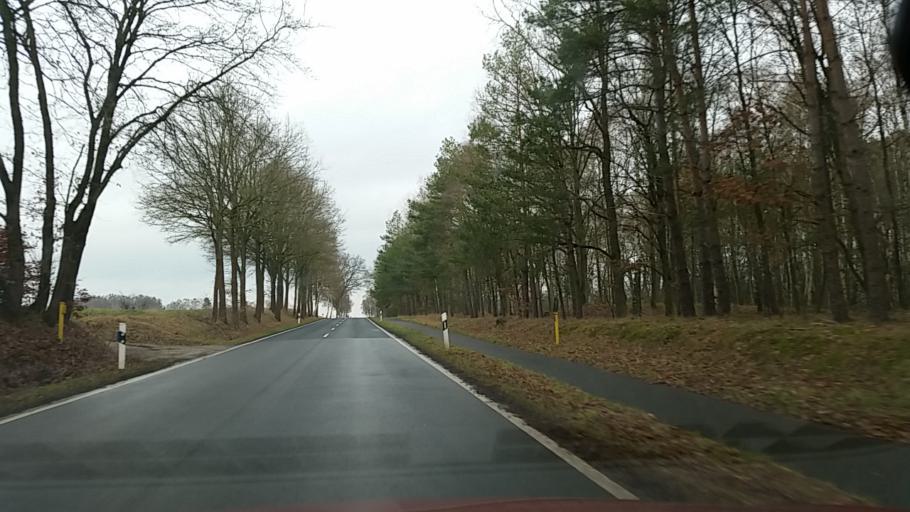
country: DE
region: Lower Saxony
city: Bispingen
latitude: 53.1074
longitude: 10.0023
